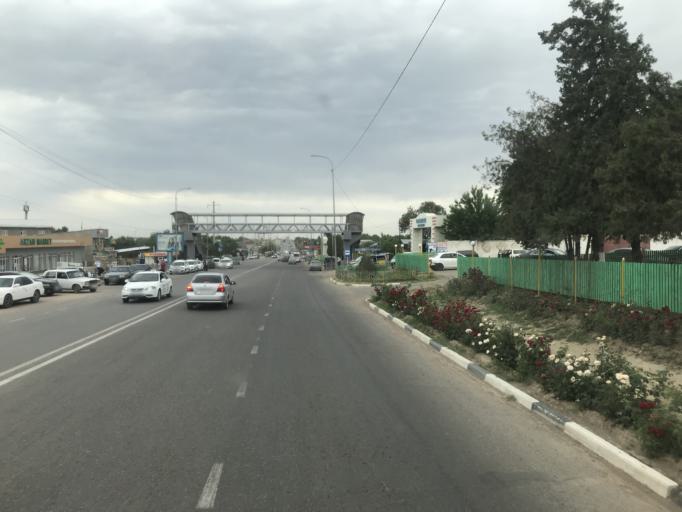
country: KZ
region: Ongtustik Qazaqstan
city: Saryaghash
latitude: 41.4633
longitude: 69.1578
